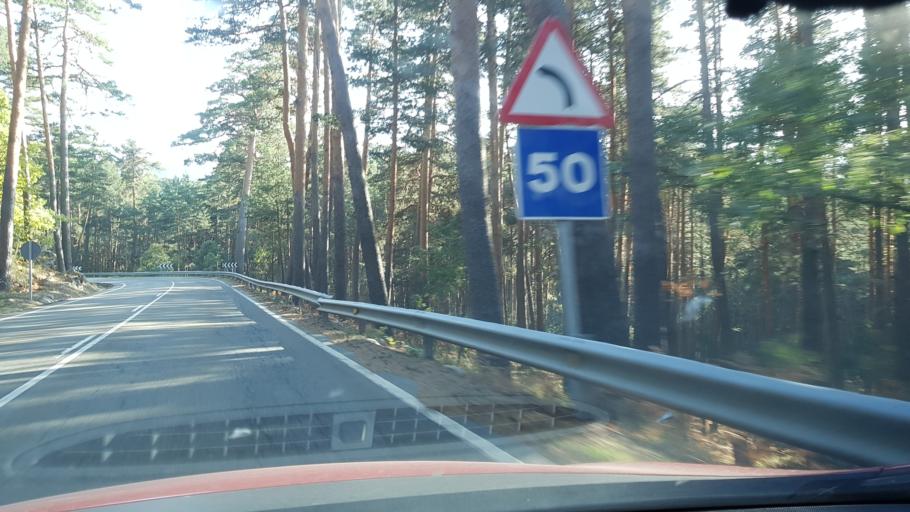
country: ES
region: Castille and Leon
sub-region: Provincia de Segovia
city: San Ildefonso
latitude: 40.8275
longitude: -4.0226
